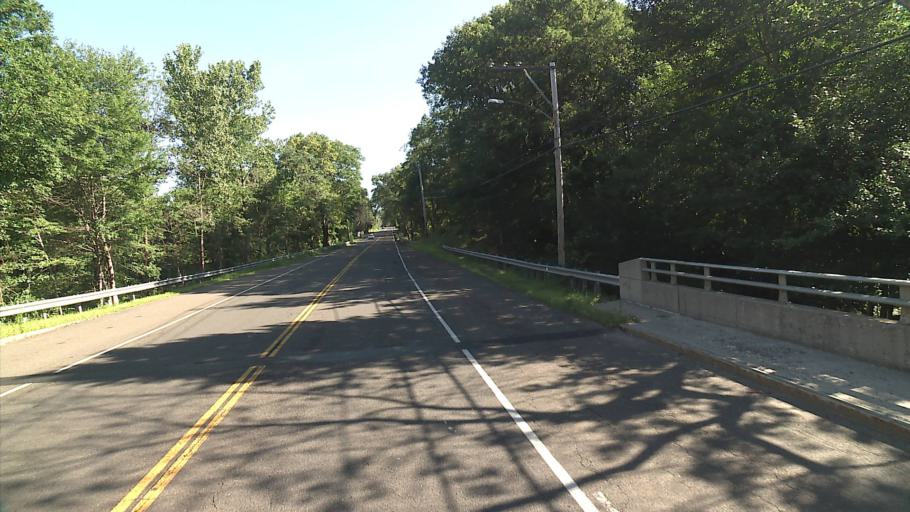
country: US
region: Connecticut
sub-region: New Haven County
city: Cheshire
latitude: 41.4490
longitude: -72.9098
